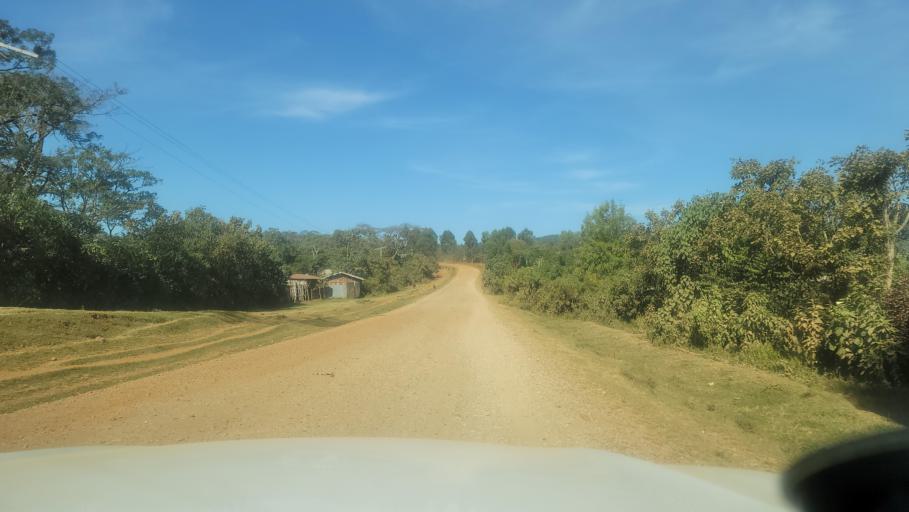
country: ET
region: Oromiya
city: Agaro
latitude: 7.7963
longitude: 36.4920
